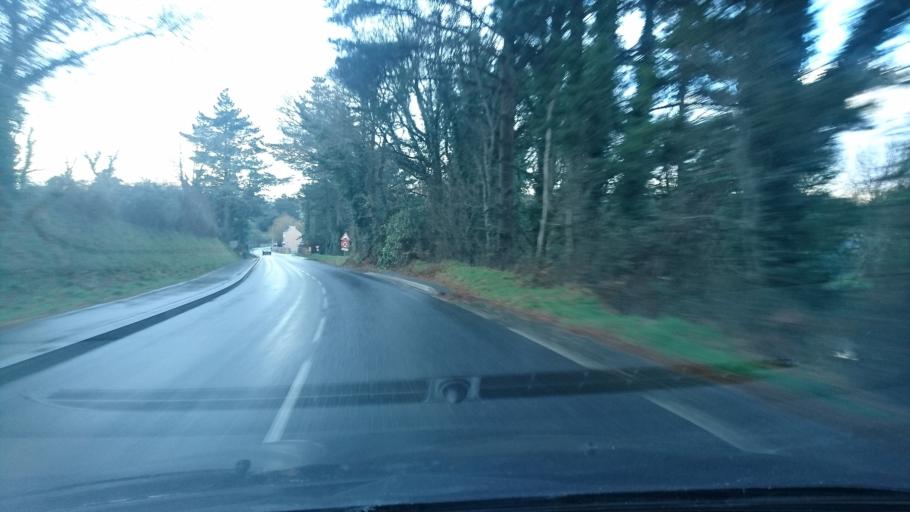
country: FR
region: Brittany
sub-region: Departement du Finistere
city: Guilers
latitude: 48.4015
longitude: -4.5416
